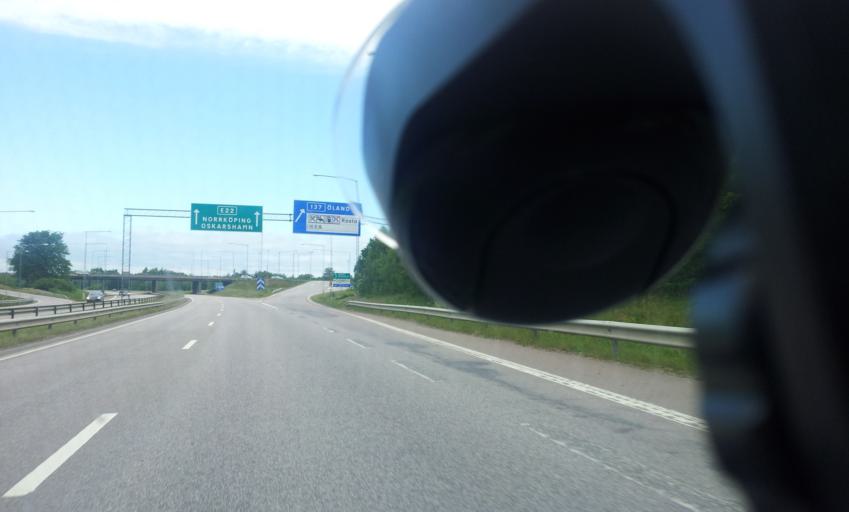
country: SE
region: Kalmar
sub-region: Kalmar Kommun
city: Kalmar
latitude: 56.6800
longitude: 16.3286
